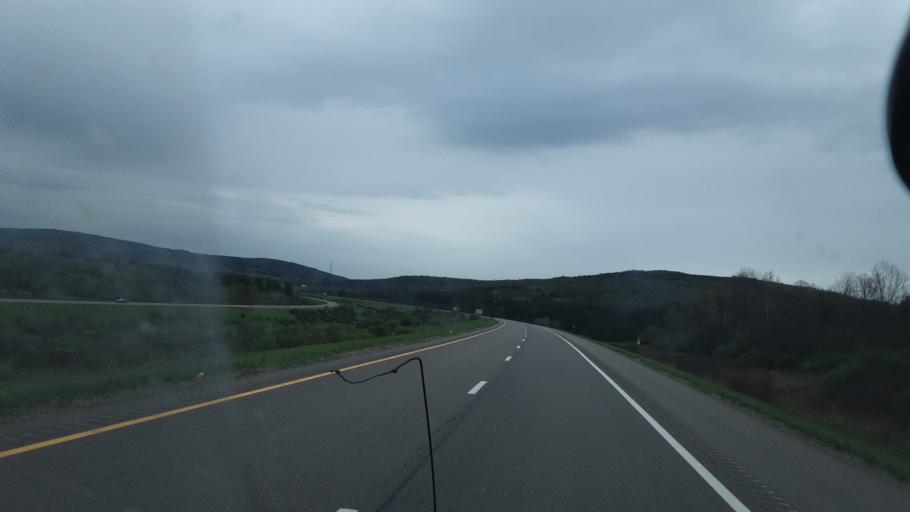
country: US
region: New York
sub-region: Allegany County
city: Belmont
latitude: 42.2928
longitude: -77.9838
